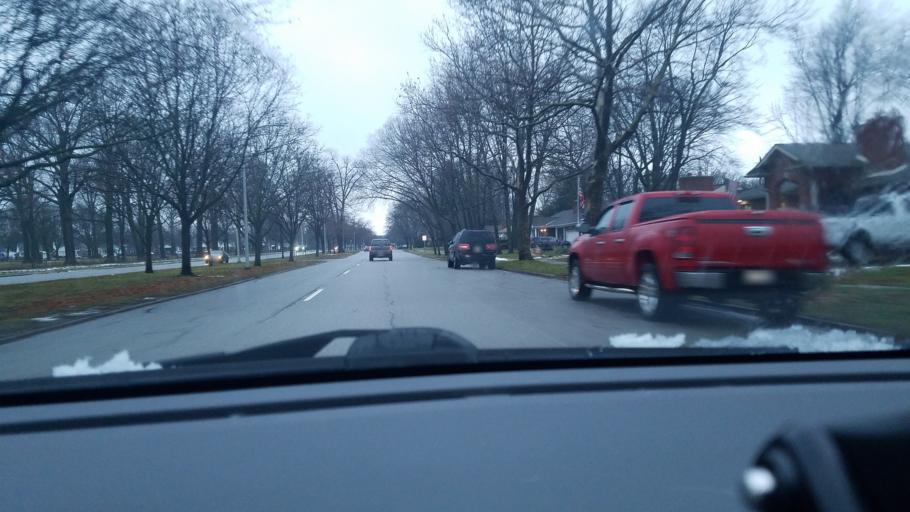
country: US
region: Michigan
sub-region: Wayne County
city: Allen Park
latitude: 42.2867
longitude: -83.2368
